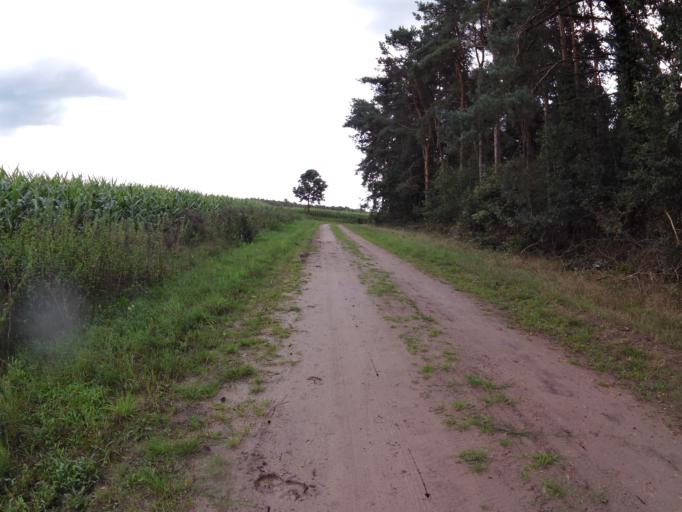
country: DE
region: Lower Saxony
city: Sandbostel
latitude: 53.3776
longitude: 9.1477
